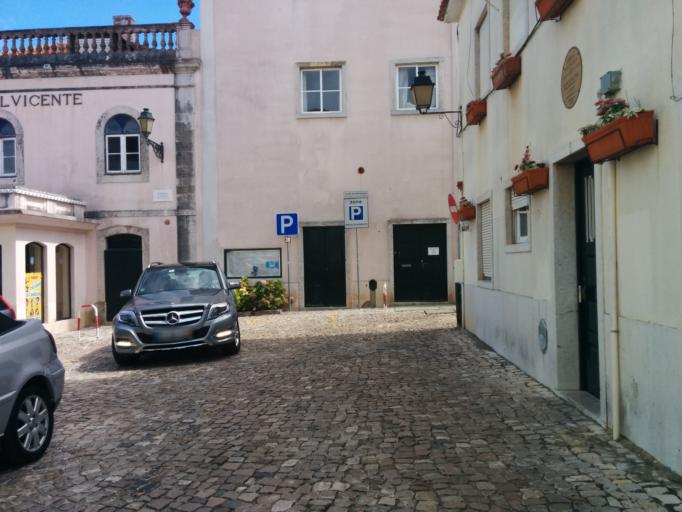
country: PT
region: Lisbon
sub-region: Cascais
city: Cascais
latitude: 38.6964
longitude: -9.4218
